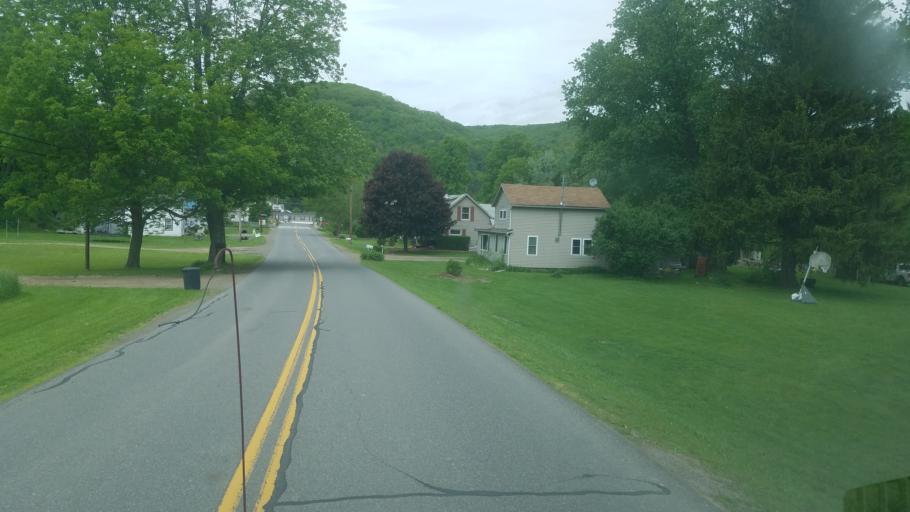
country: US
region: Pennsylvania
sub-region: Tioga County
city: Westfield
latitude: 41.9111
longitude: -77.6039
